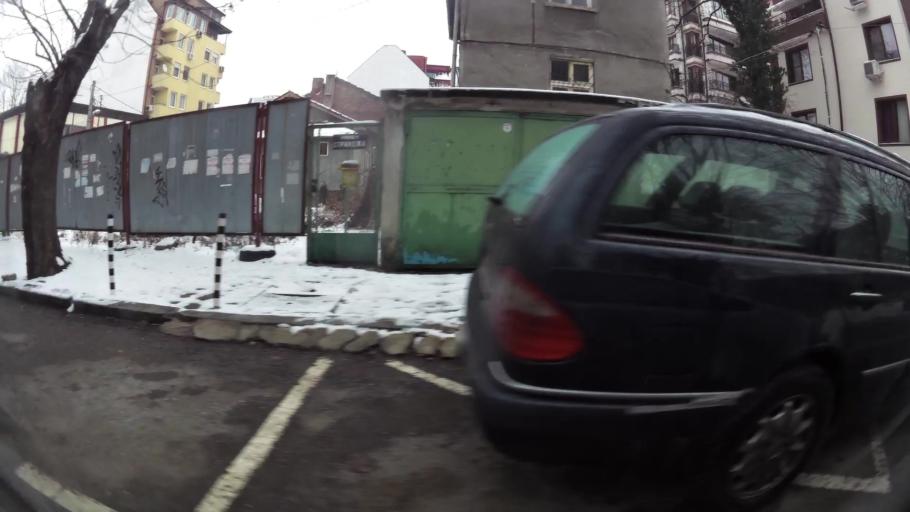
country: BG
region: Sofia-Capital
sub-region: Stolichna Obshtina
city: Sofia
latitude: 42.7113
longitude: 23.3165
